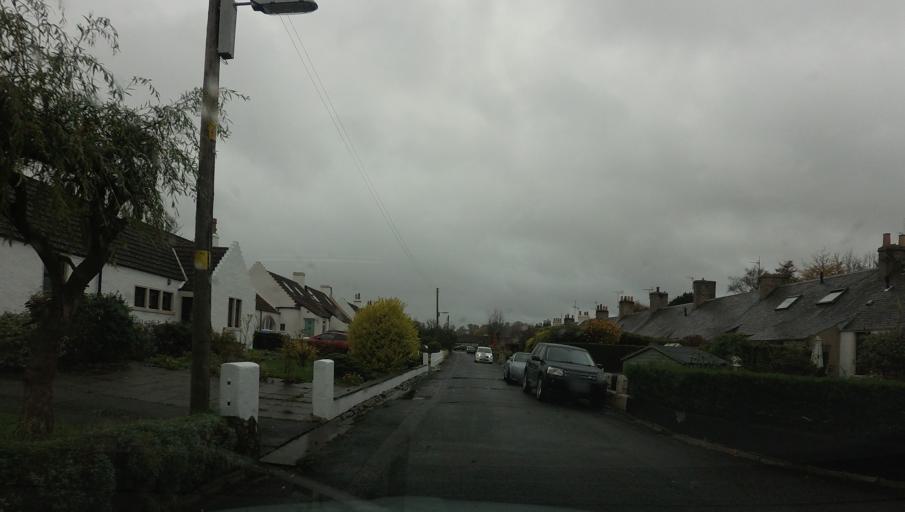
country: GB
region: Scotland
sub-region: Fife
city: East Wemyss
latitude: 56.1557
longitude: -3.0708
